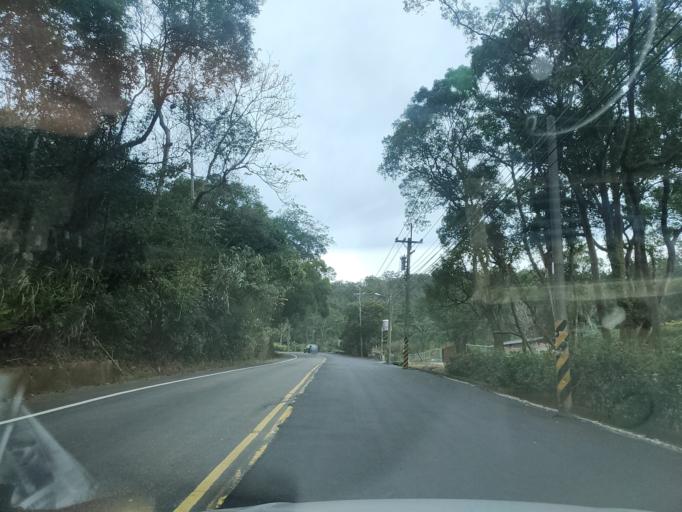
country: TW
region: Taiwan
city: Fengyuan
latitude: 24.3735
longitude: 120.7692
